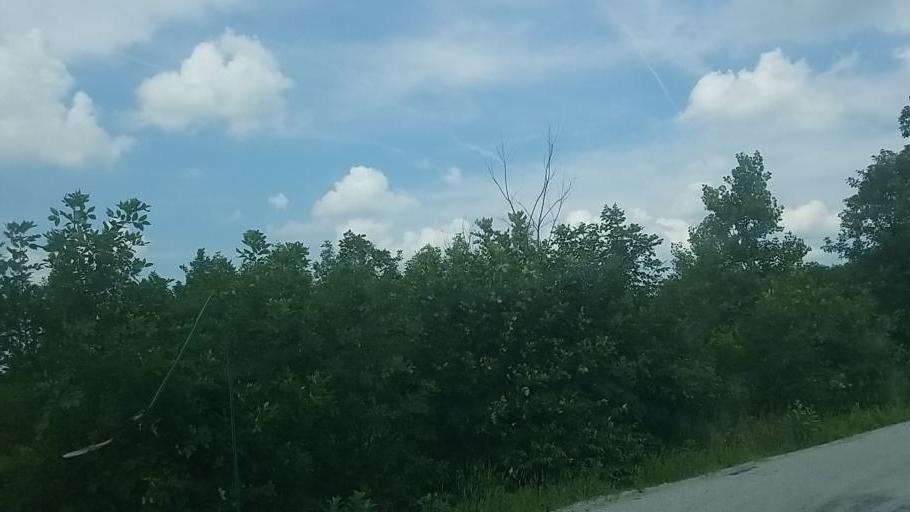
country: US
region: Ohio
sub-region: Hardin County
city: Forest
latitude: 40.7530
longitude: -83.6023
